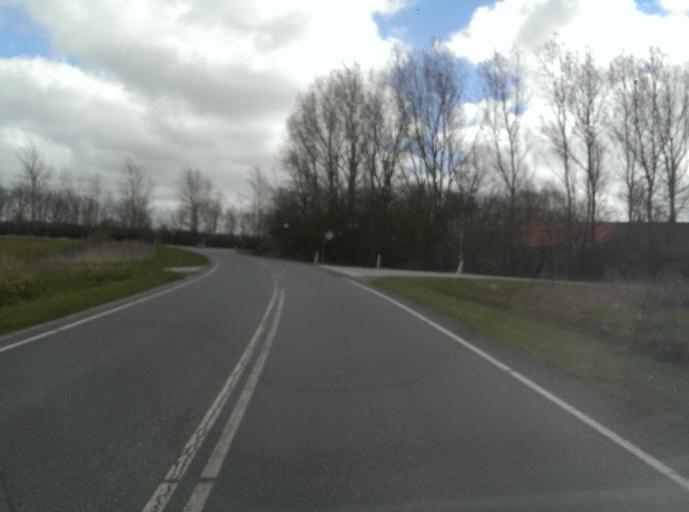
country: DK
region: South Denmark
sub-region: Esbjerg Kommune
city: Esbjerg
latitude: 55.5240
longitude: 8.4062
